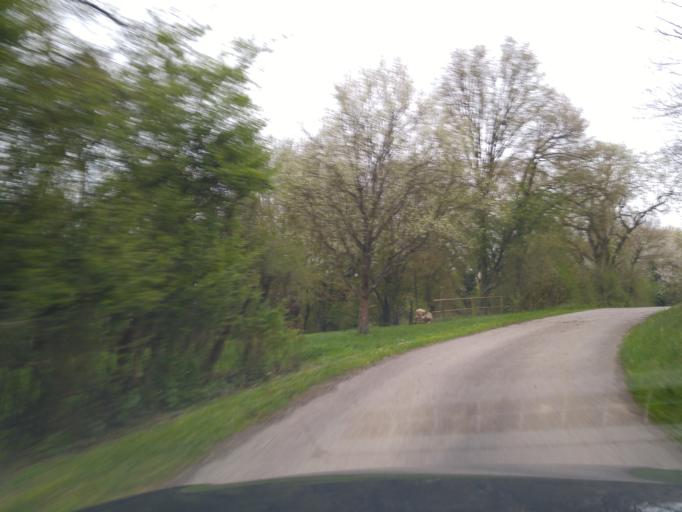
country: DE
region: Baden-Wuerttemberg
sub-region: Karlsruhe Region
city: Hassmersheim
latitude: 49.2959
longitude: 9.1284
